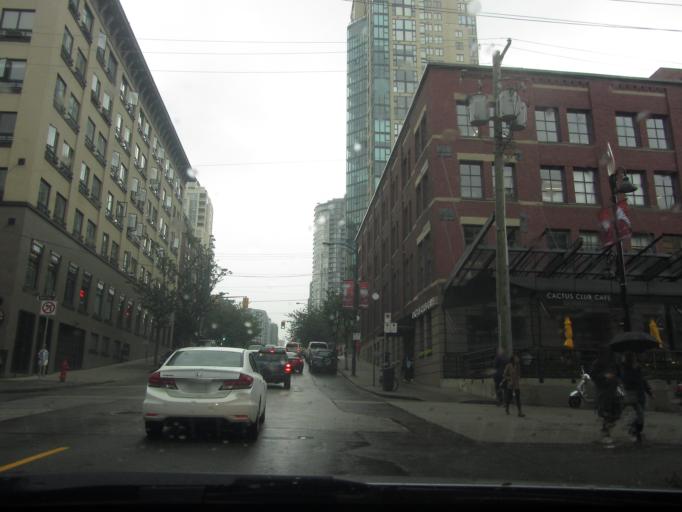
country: CA
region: British Columbia
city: West End
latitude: 49.2749
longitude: -123.1225
